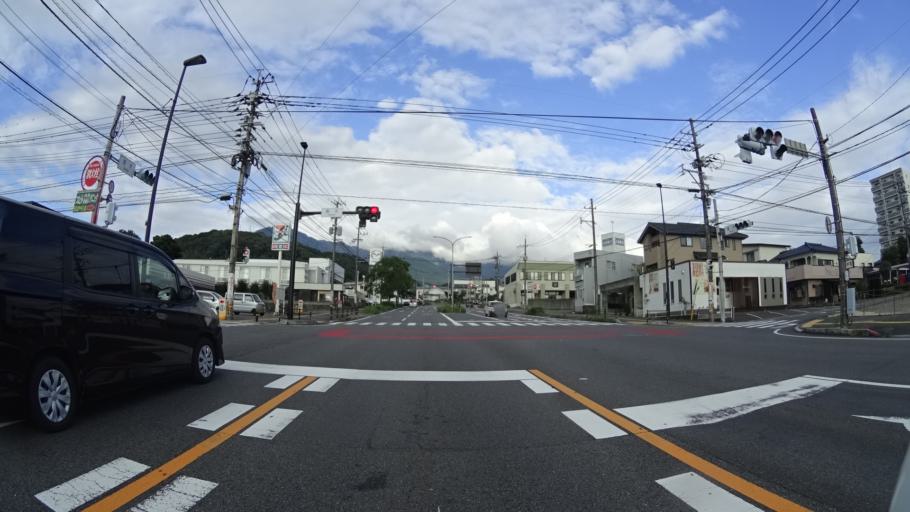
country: JP
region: Oita
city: Beppu
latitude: 33.3054
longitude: 131.4918
